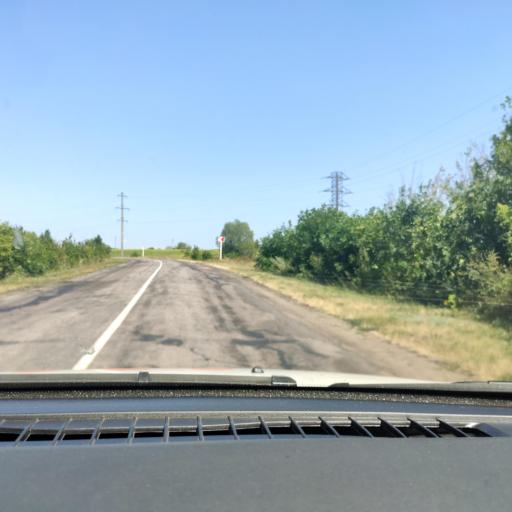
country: RU
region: Voronezj
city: Ol'khovatka
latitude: 50.6048
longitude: 39.3150
